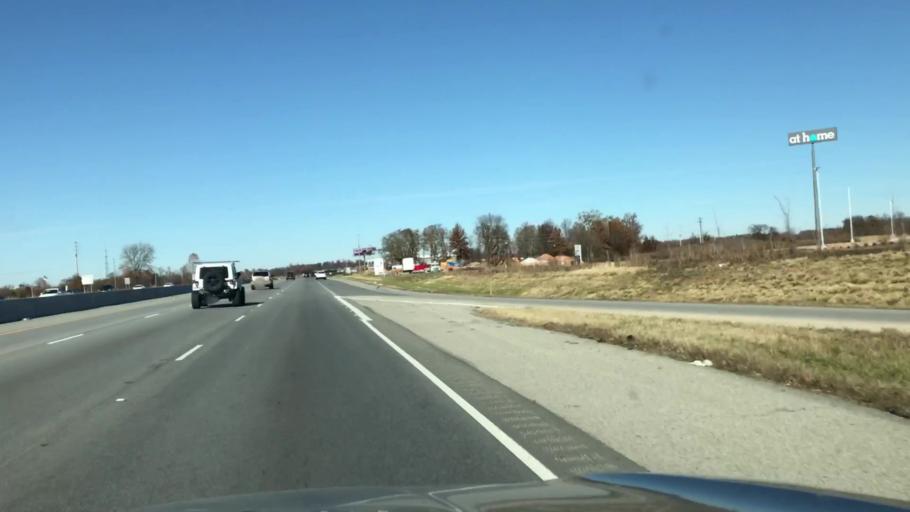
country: US
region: Arkansas
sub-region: Benton County
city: Lowell
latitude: 36.2853
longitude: -94.1578
